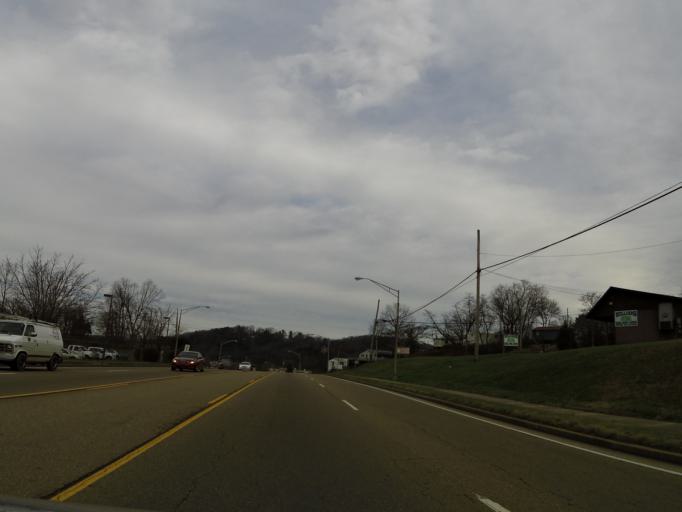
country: US
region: Tennessee
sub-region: Cocke County
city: Newport
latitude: 35.9641
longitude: -83.1940
